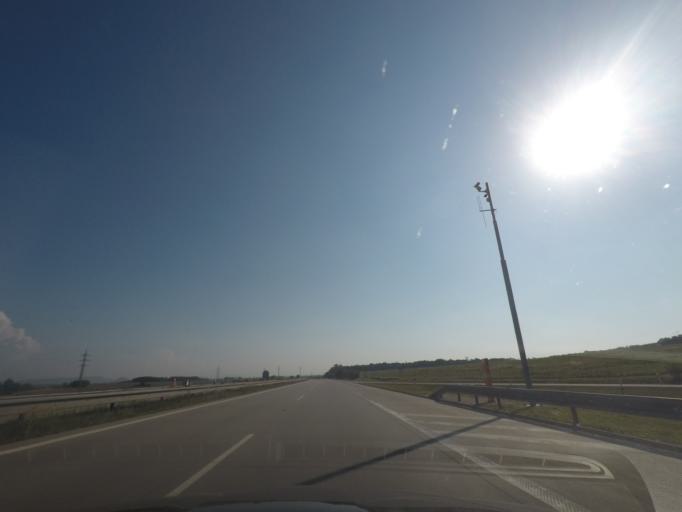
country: CZ
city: Bilovec
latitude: 49.7271
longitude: 18.0161
